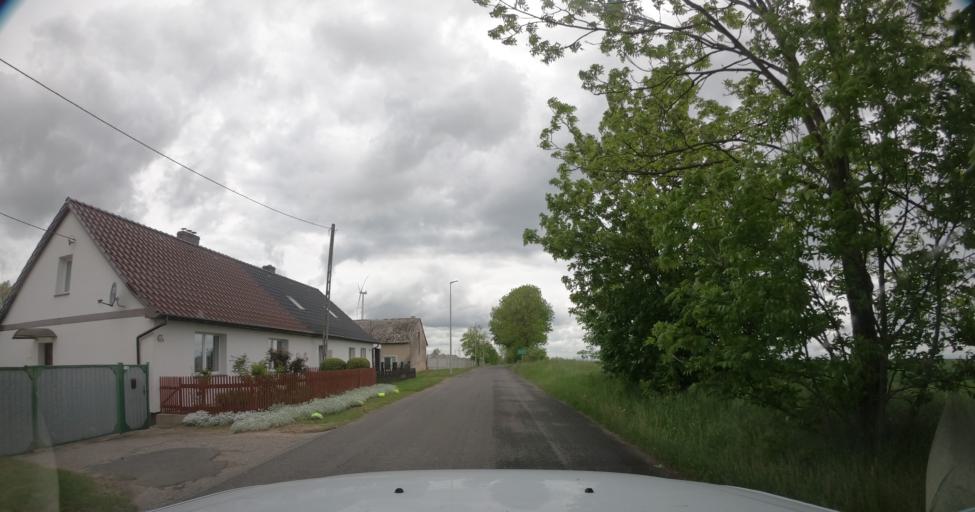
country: PL
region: West Pomeranian Voivodeship
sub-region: Powiat pyrzycki
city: Kozielice
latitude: 53.1116
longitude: 14.8147
